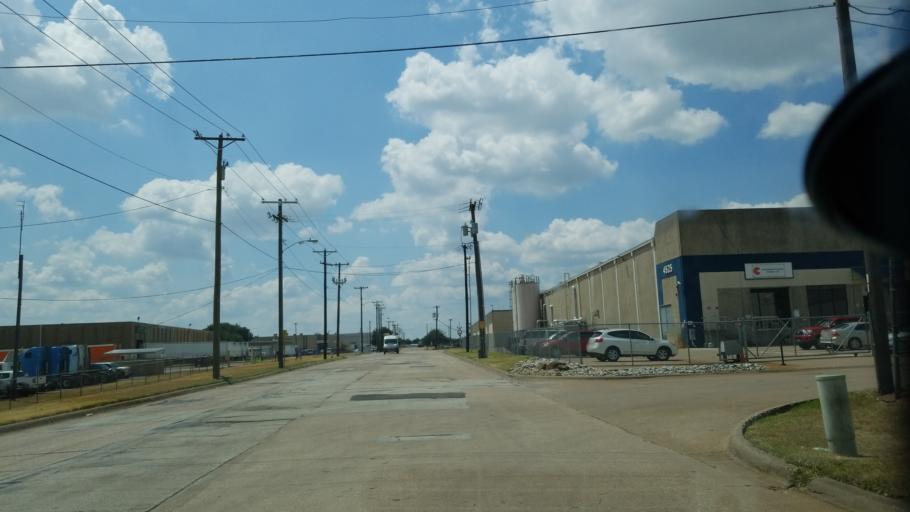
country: US
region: Texas
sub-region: Dallas County
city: Duncanville
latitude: 32.6895
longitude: -96.8987
